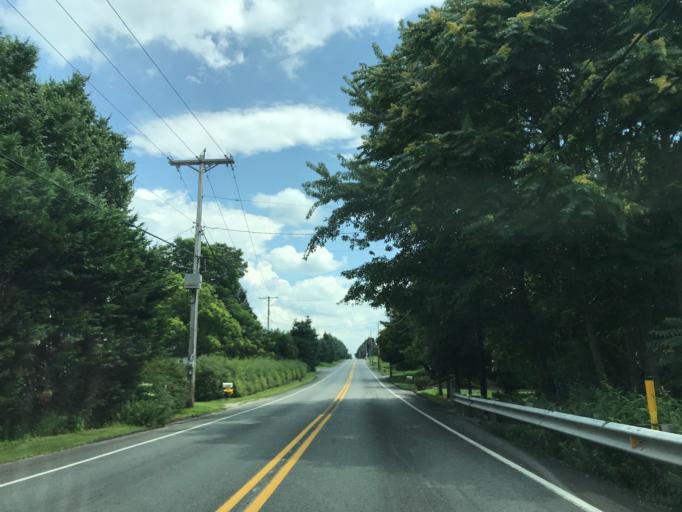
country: US
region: Pennsylvania
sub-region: York County
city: Windsor
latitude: 39.8932
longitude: -76.5607
